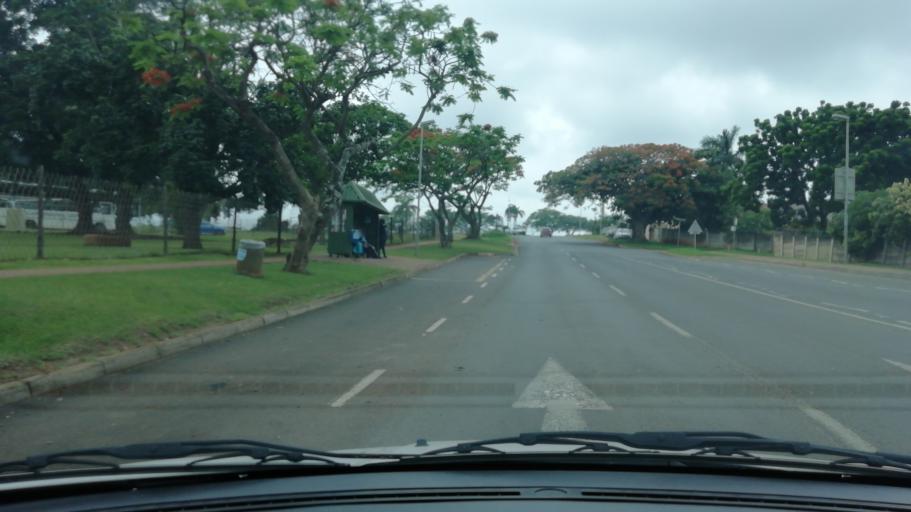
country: ZA
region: KwaZulu-Natal
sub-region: uThungulu District Municipality
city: Empangeni
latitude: -28.7593
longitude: 31.9001
